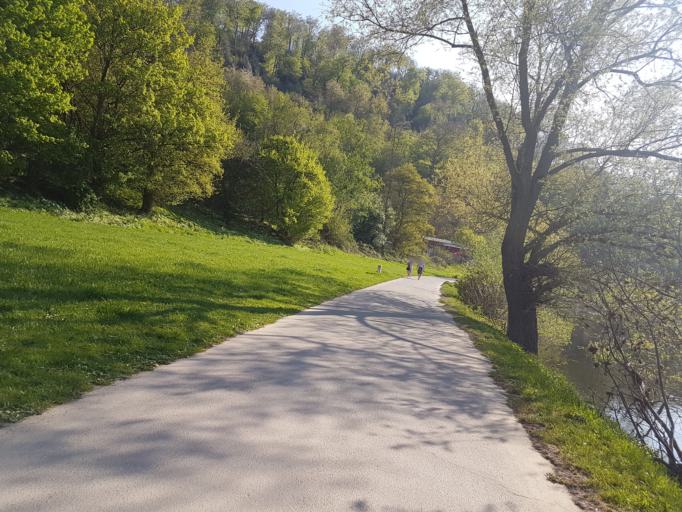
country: DE
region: North Rhine-Westphalia
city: Hattingen
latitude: 51.3886
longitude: 7.1625
